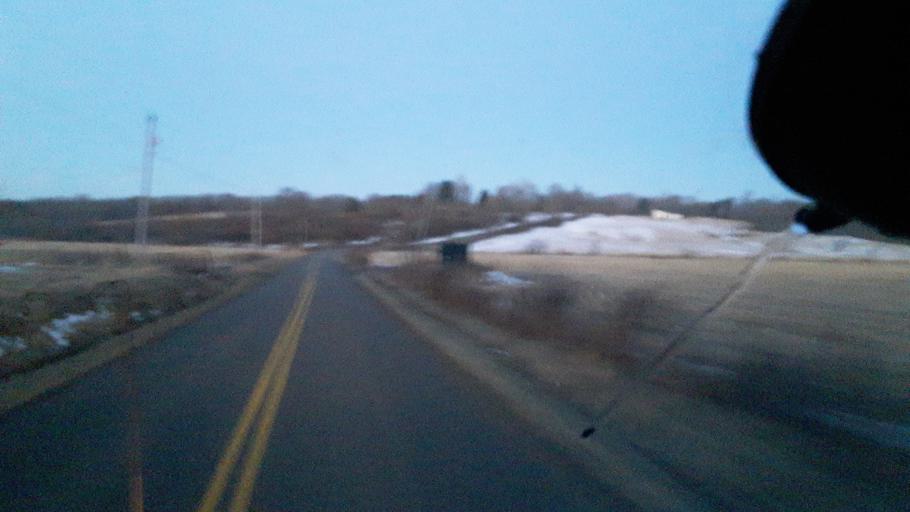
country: US
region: Ohio
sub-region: Perry County
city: New Lexington
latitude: 39.7100
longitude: -82.2258
